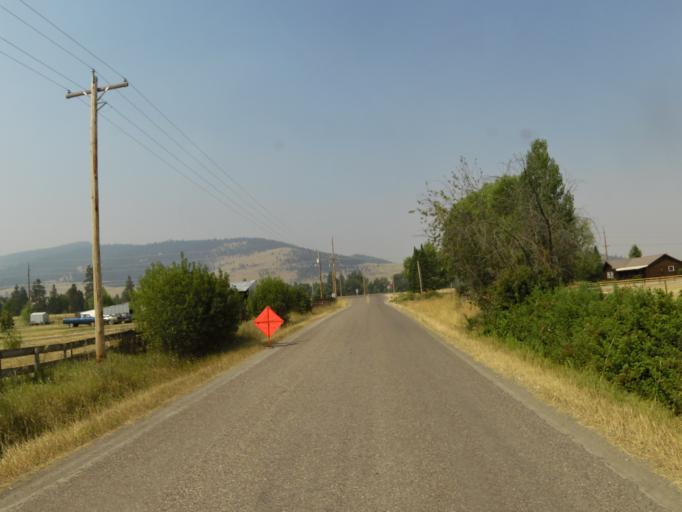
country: US
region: Montana
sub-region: Missoula County
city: Frenchtown
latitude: 47.1890
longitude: -114.1005
